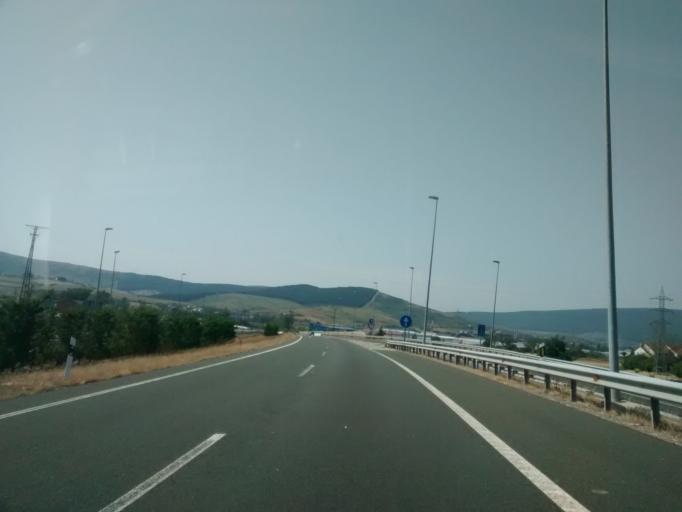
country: ES
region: Cantabria
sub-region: Provincia de Cantabria
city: Reinosa
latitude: 43.0060
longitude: -4.1261
